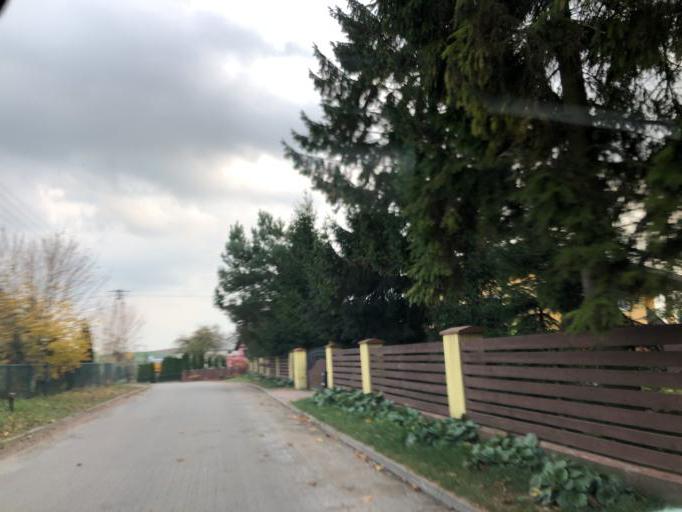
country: PL
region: Podlasie
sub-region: Lomza
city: Lomza
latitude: 53.1218
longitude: 22.0106
